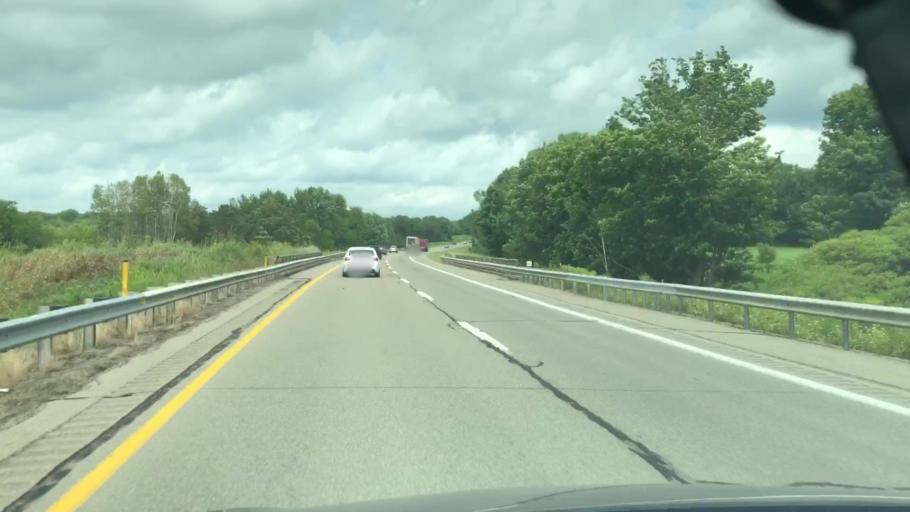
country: US
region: Pennsylvania
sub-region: Erie County
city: Edinboro
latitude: 41.7649
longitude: -80.1944
